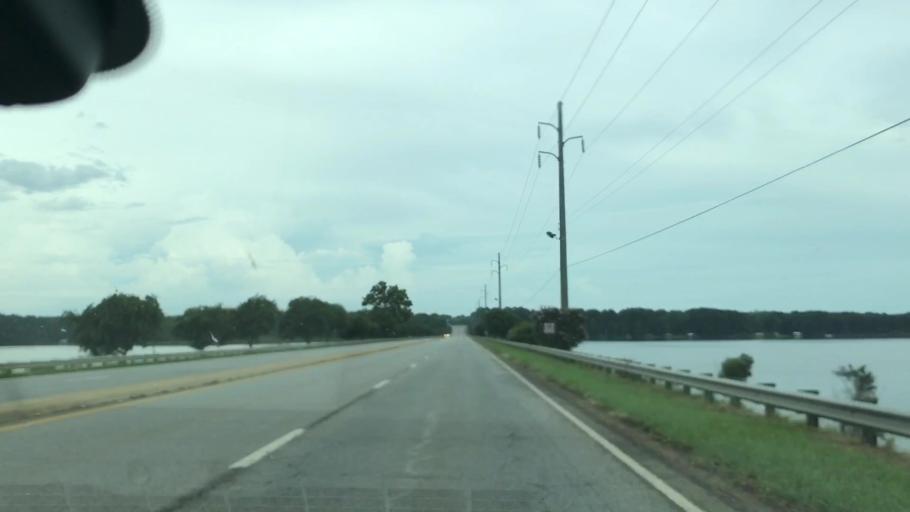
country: US
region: Georgia
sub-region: Quitman County
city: Georgetown
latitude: 31.8902
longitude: -85.1235
